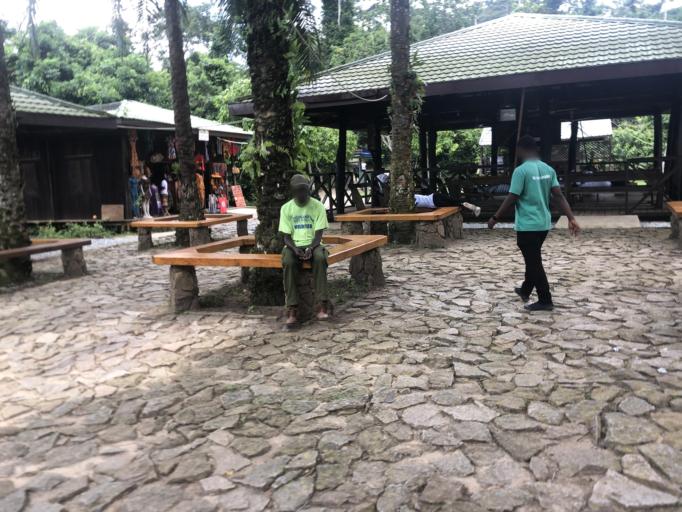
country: GH
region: Central
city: Elmina
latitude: 5.3488
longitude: -1.3836
